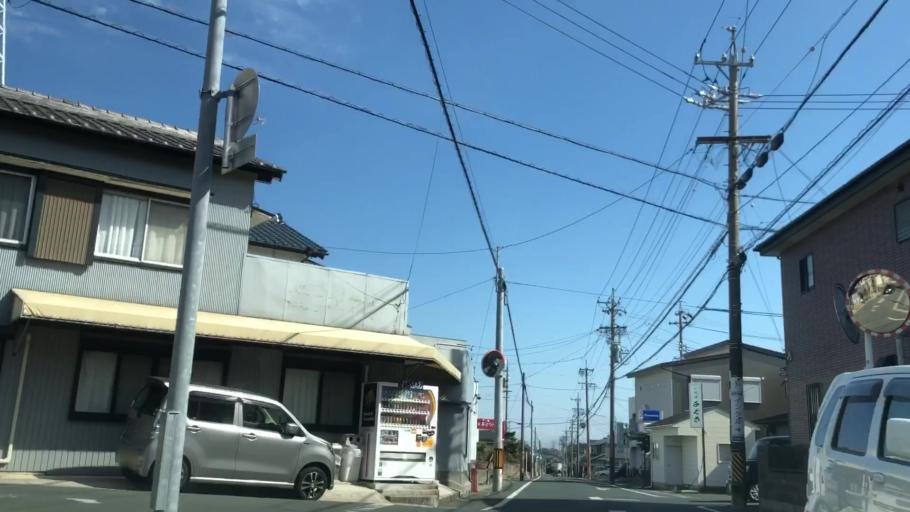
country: JP
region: Aichi
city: Toyohashi
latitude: 34.7229
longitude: 137.4001
